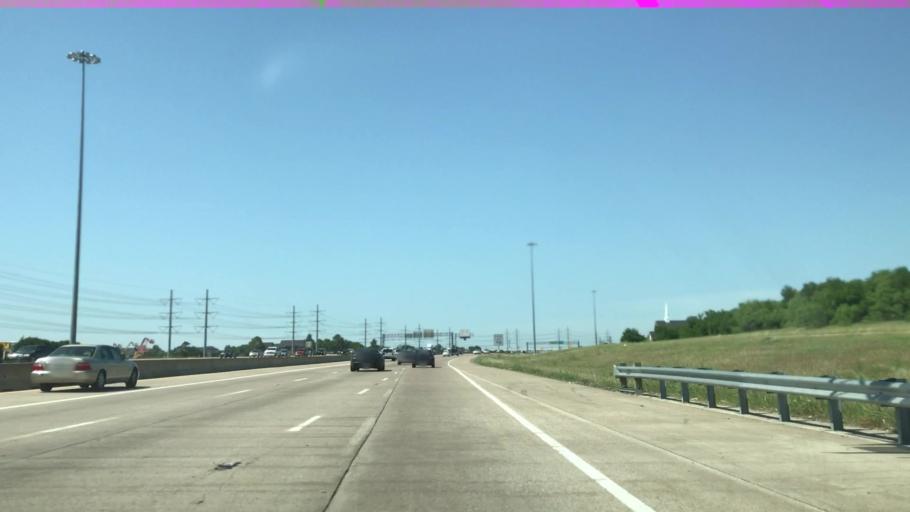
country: US
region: Texas
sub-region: Tarrant County
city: Euless
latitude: 32.8473
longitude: -97.0166
